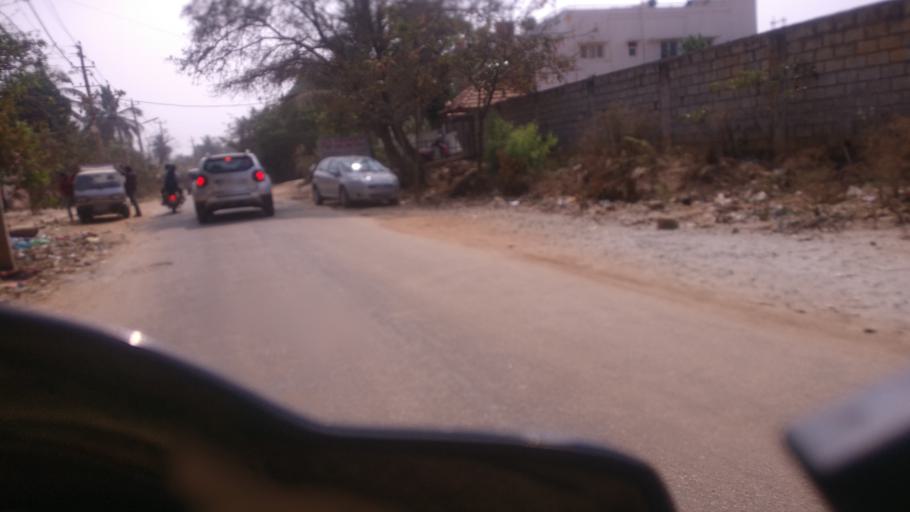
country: IN
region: Karnataka
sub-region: Bangalore Urban
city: Bangalore
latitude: 12.8994
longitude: 77.6861
